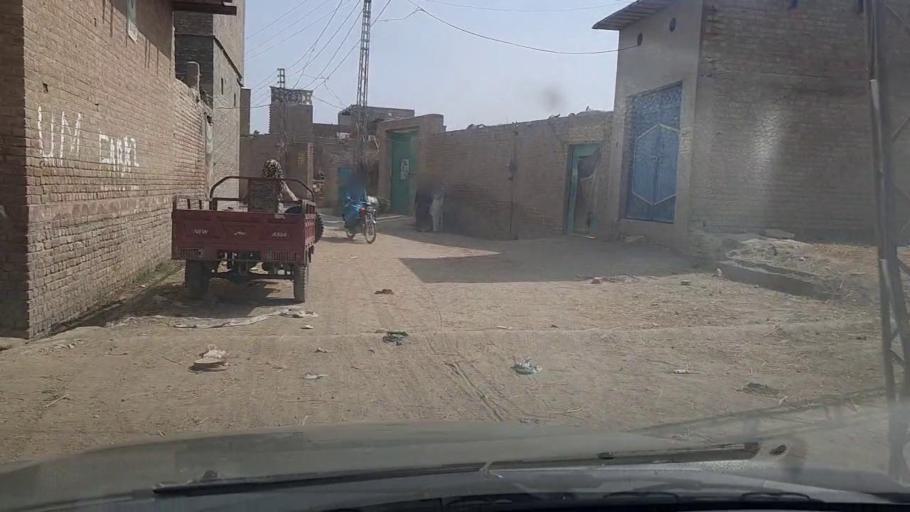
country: PK
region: Sindh
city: Chak
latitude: 27.8300
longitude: 68.7757
